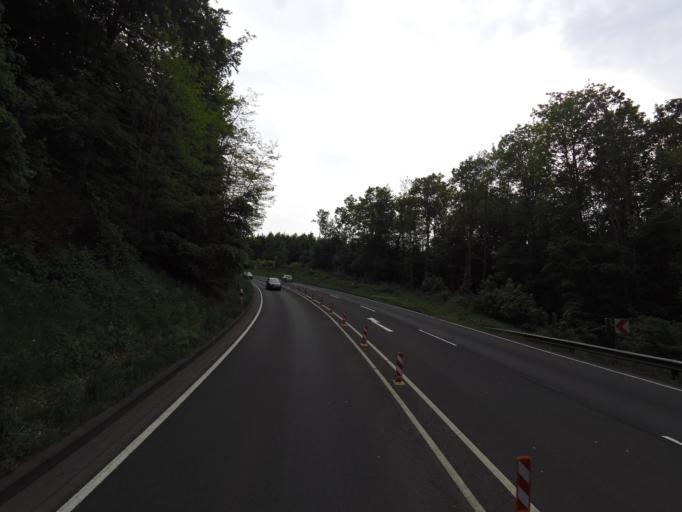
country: DE
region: Rheinland-Pfalz
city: Waldesch
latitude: 50.3148
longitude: 7.5531
